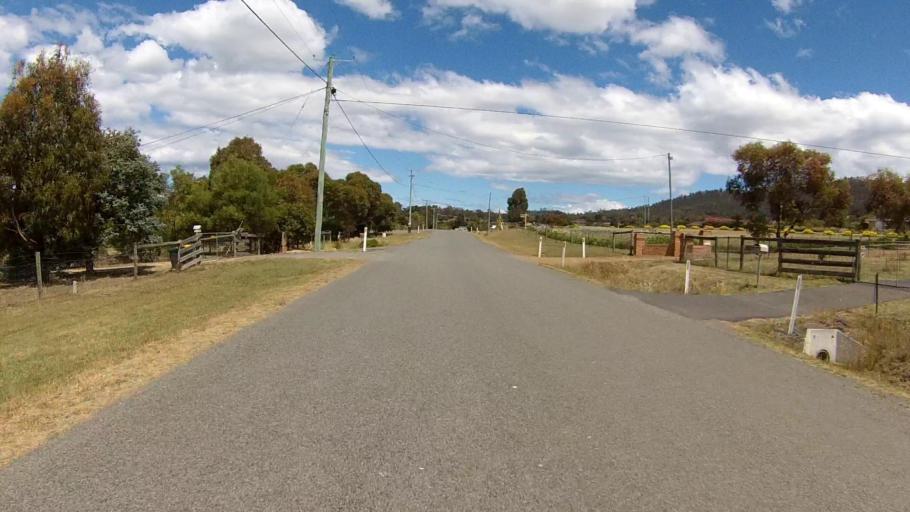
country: AU
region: Tasmania
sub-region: Clarence
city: Seven Mile Beach
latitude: -42.8514
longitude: 147.4800
